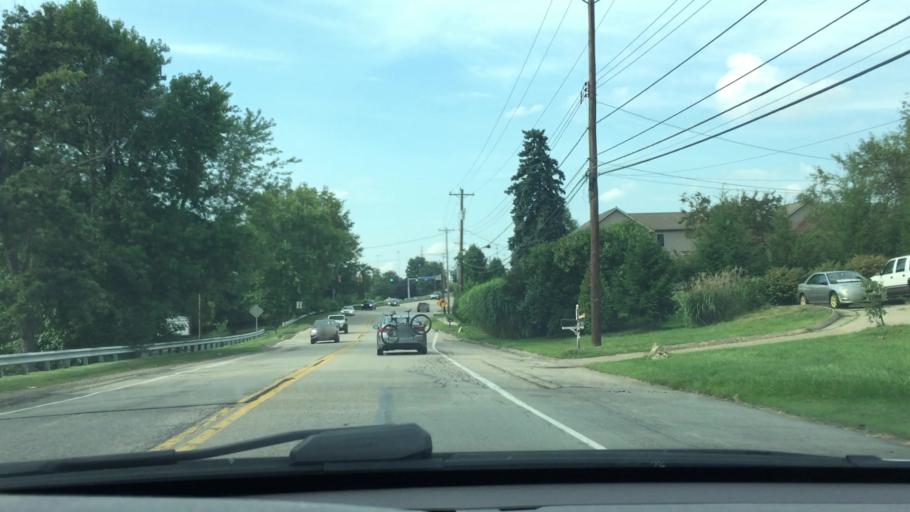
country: US
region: Pennsylvania
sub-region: Allegheny County
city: Pitcairn
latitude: 40.4264
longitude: -79.7508
